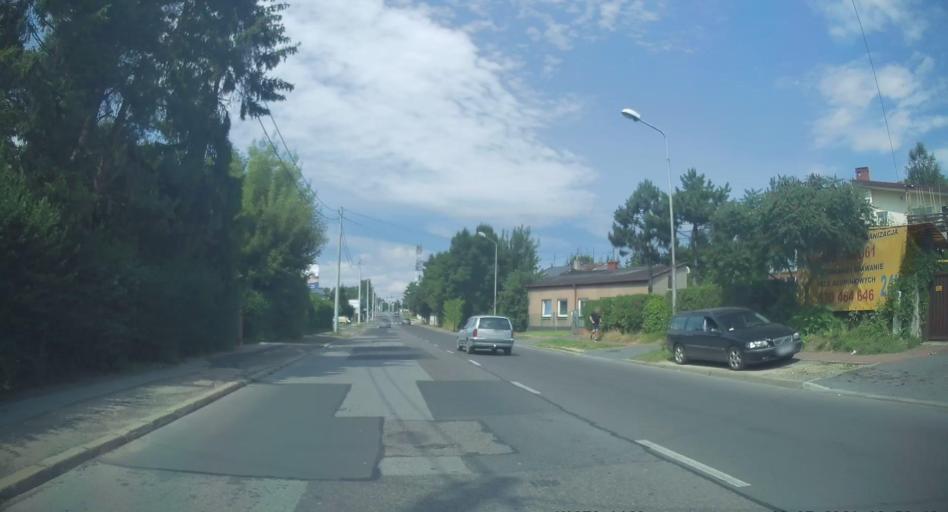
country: PL
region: Silesian Voivodeship
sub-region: Czestochowa
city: Czestochowa
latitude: 50.8111
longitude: 19.0833
